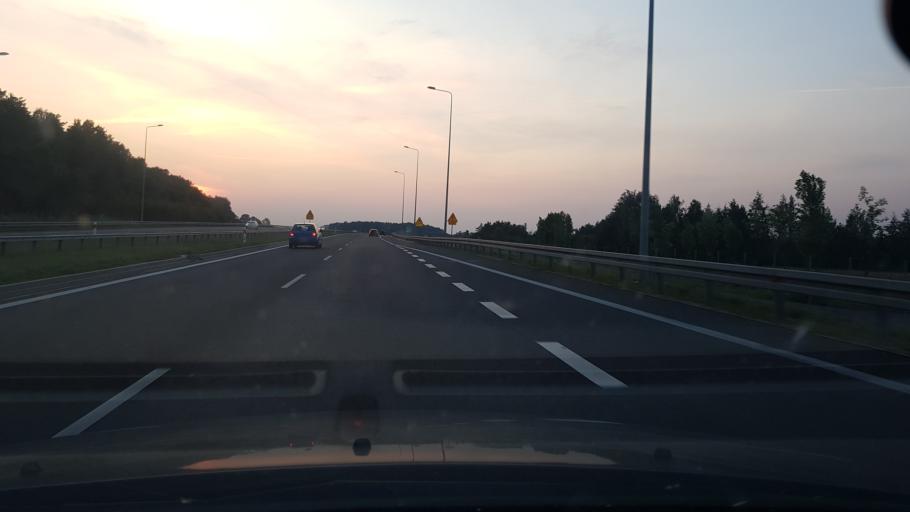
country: PL
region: Warmian-Masurian Voivodeship
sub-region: Powiat nidzicki
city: Nidzica
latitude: 53.3747
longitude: 20.3809
